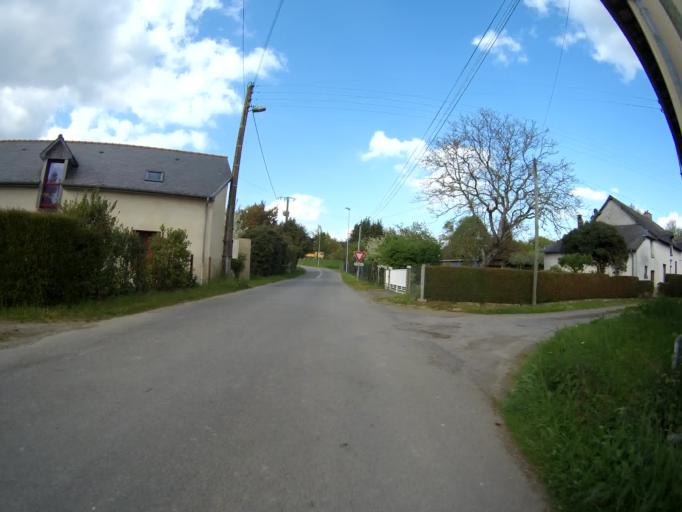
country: FR
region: Brittany
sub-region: Departement d'Ille-et-Vilaine
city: Vern-sur-Seiche
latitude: 48.0731
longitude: -1.5786
